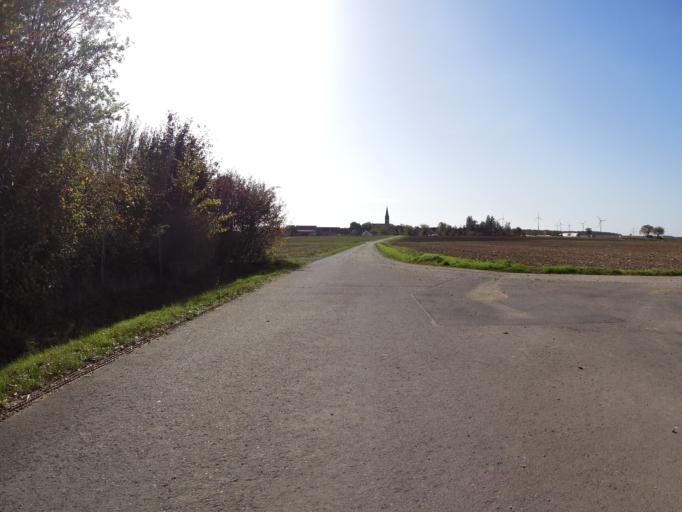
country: DE
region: Bavaria
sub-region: Regierungsbezirk Unterfranken
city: Biebelried
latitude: 49.7512
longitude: 10.0630
